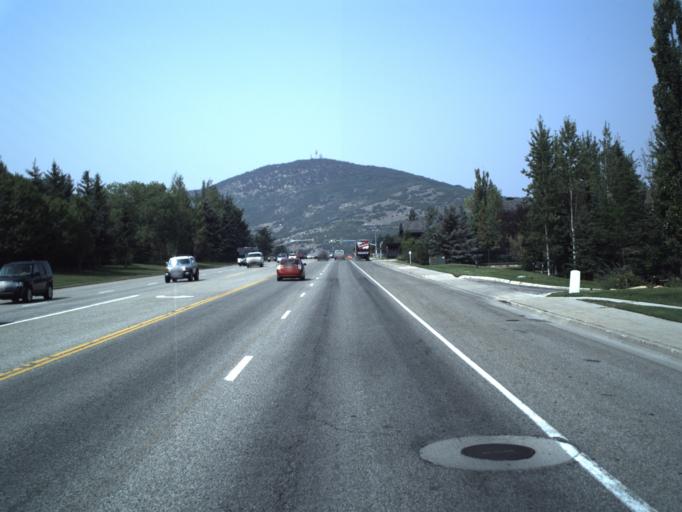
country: US
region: Utah
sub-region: Summit County
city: Park City
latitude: 40.6654
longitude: -111.5140
